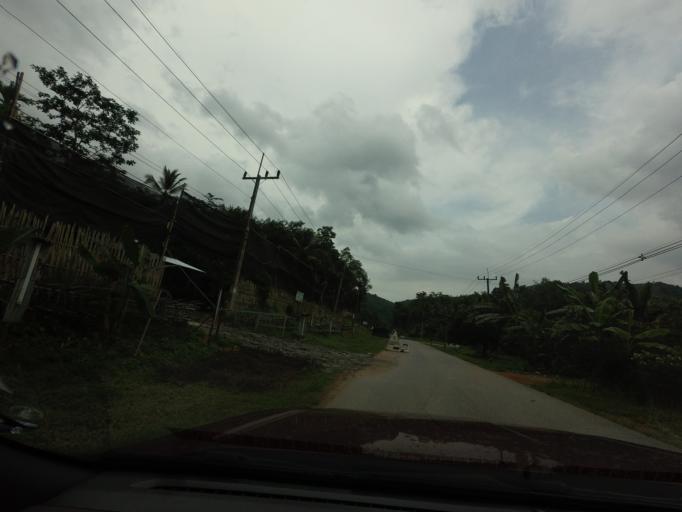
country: TH
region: Yala
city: Than To
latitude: 6.1968
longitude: 101.2419
